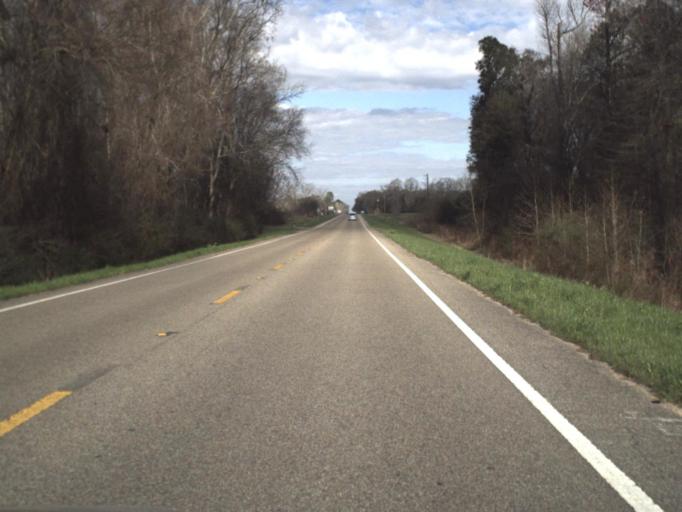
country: US
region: Florida
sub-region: Jackson County
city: Malone
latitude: 30.9969
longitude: -85.1990
